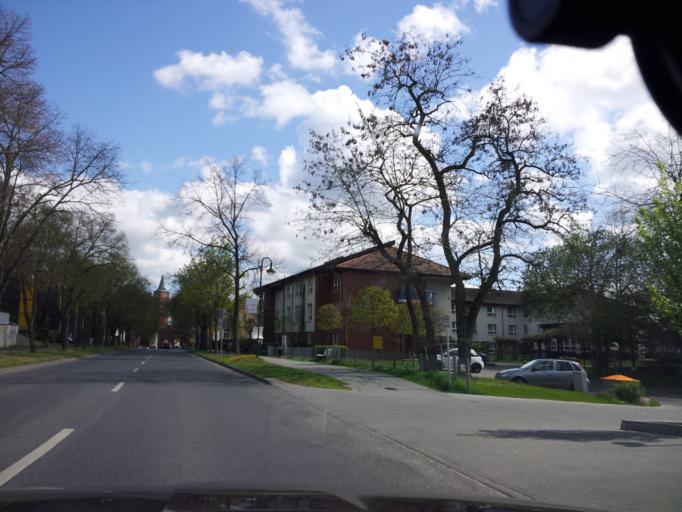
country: DE
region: Brandenburg
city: Bernau bei Berlin
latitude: 52.6818
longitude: 13.5808
